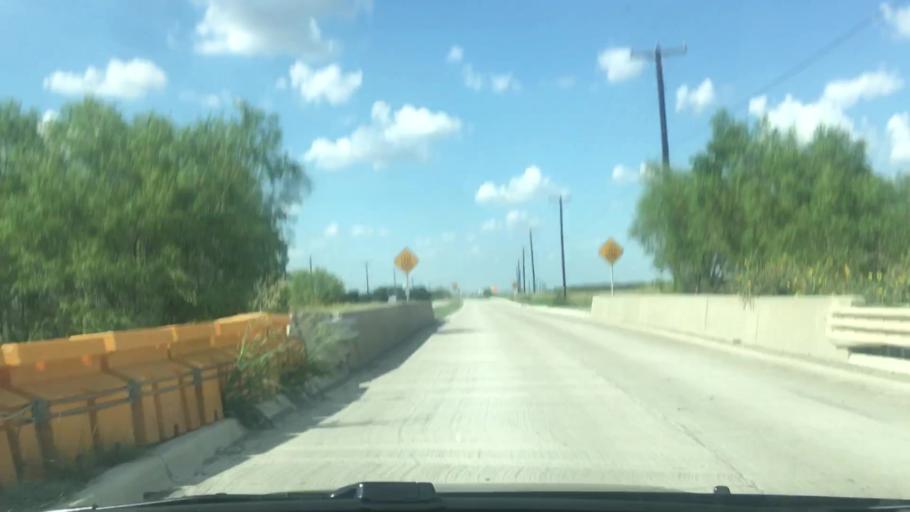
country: US
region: Texas
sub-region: Collin County
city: Prosper
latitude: 33.2199
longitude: -96.8195
